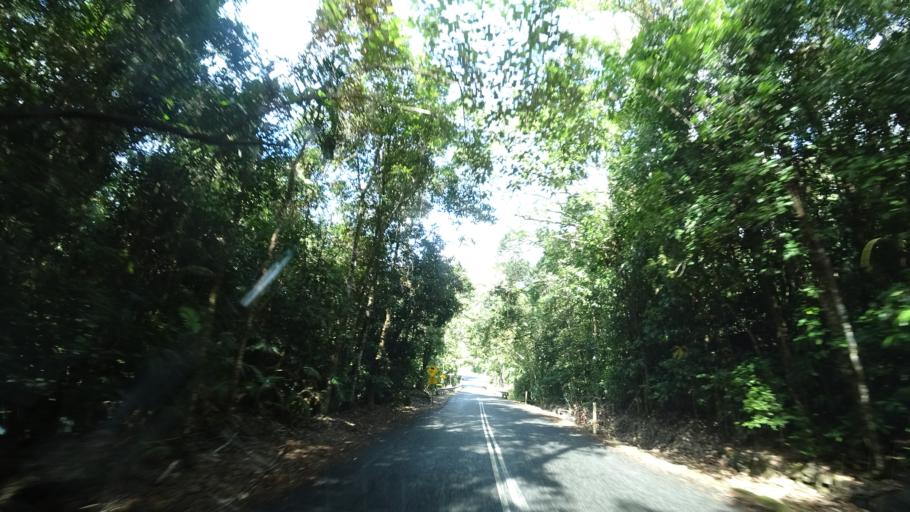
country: AU
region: Queensland
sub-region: Cairns
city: Port Douglas
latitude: -16.1392
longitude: 145.4307
